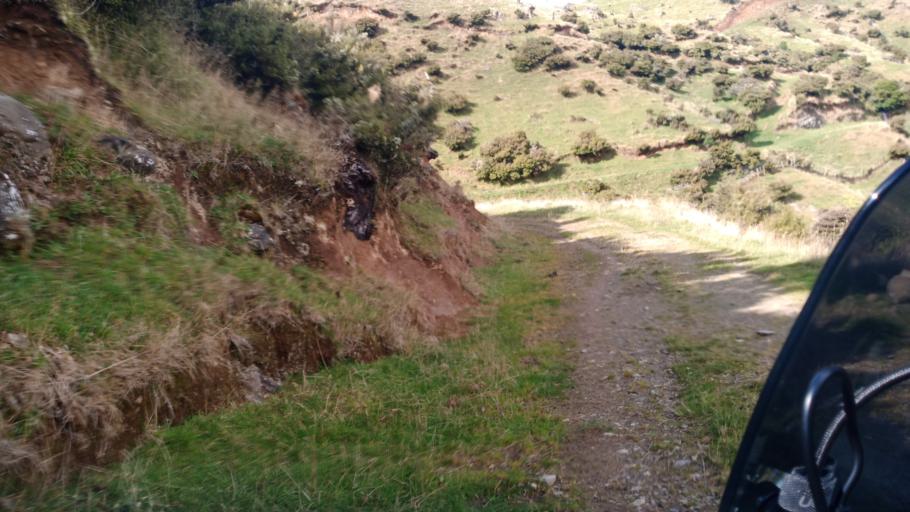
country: NZ
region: Gisborne
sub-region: Gisborne District
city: Gisborne
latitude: -38.4713
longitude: 177.5358
